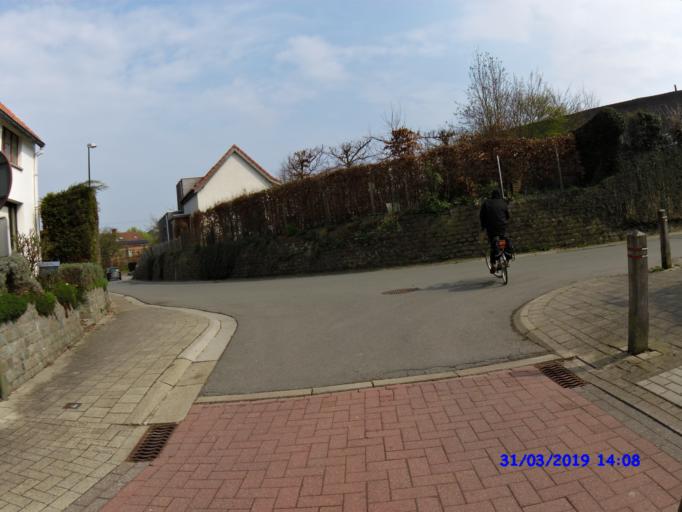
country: BE
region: Flanders
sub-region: Provincie Vlaams-Brabant
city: Asse
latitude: 50.8999
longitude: 4.2274
